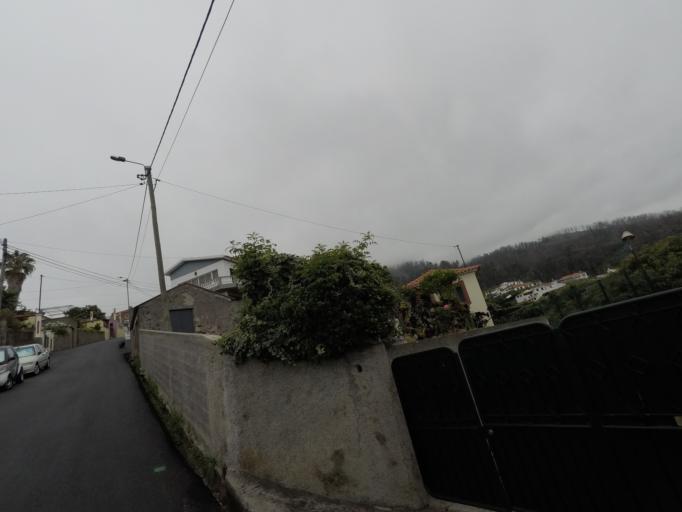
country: PT
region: Madeira
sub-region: Funchal
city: Nossa Senhora do Monte
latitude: 32.6732
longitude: -16.9386
